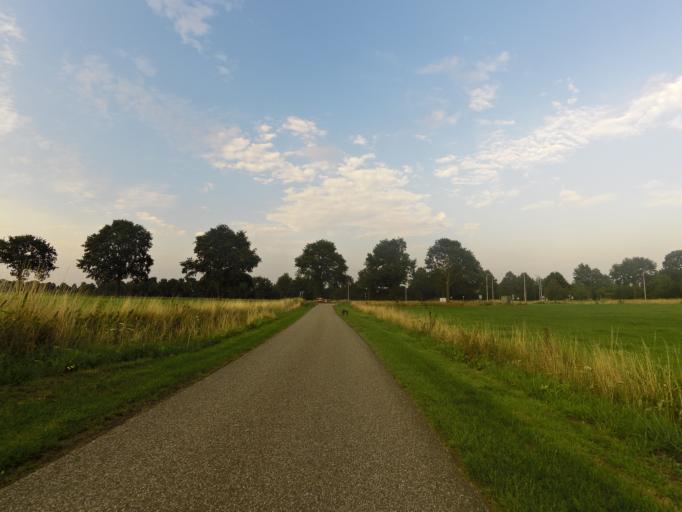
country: NL
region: Gelderland
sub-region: Oude IJsselstreek
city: Gendringen
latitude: 51.8811
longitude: 6.3681
